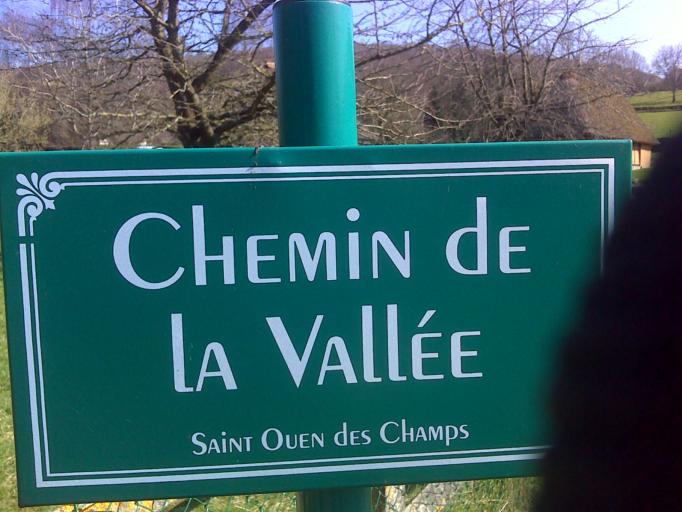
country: FR
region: Haute-Normandie
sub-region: Departement de l'Eure
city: Pont-Audemer
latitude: 49.4078
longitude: 0.5225
